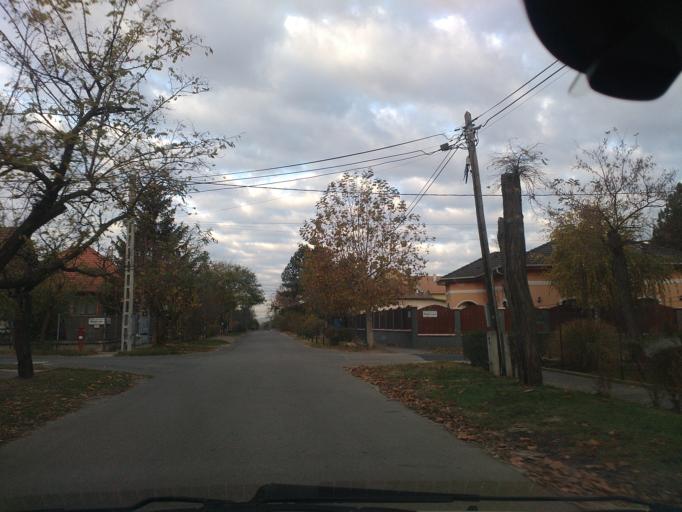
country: HU
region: Budapest
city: Budapest XVIII. keruelet
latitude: 47.4326
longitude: 19.2148
